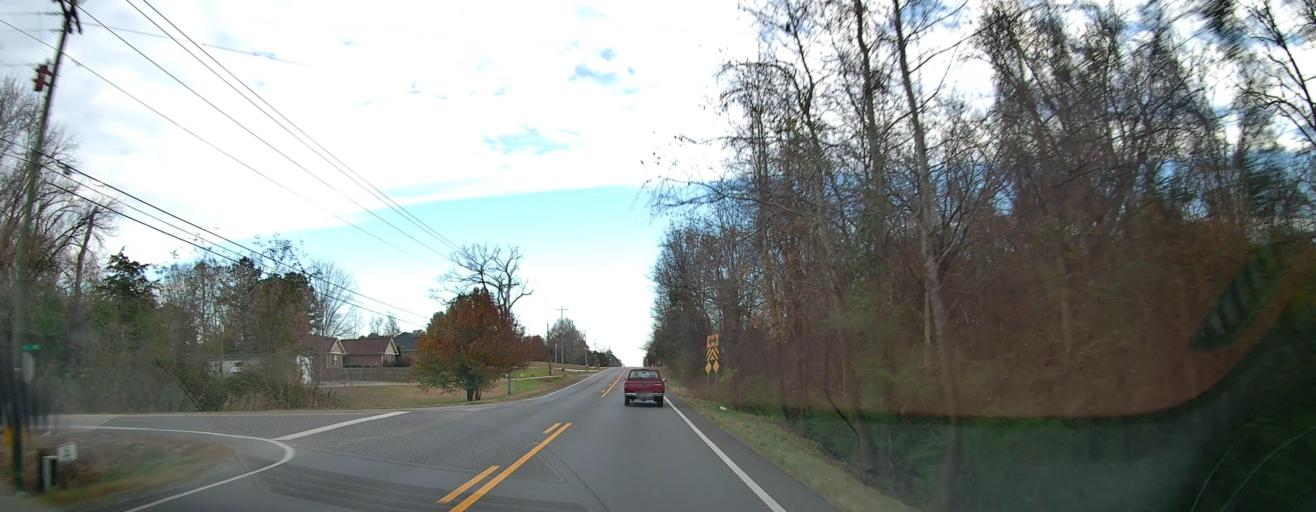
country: US
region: Alabama
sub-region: Morgan County
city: Priceville
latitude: 34.4848
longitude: -86.8304
